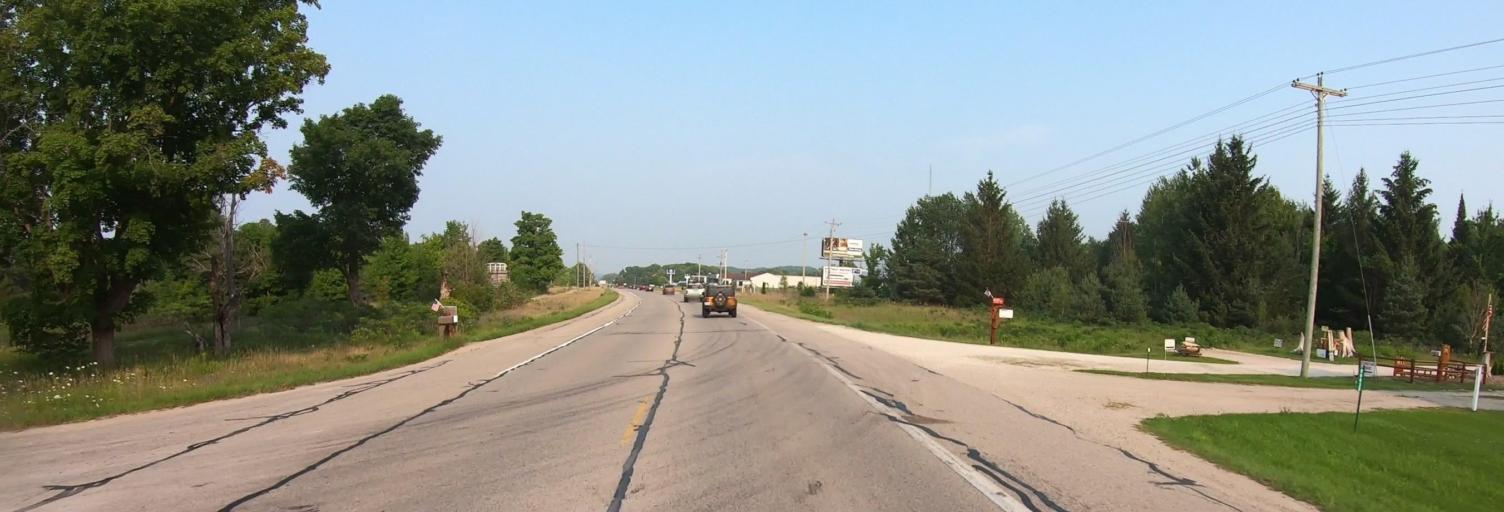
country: US
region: Michigan
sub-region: Emmet County
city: Harbor Springs
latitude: 45.3615
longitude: -85.1079
